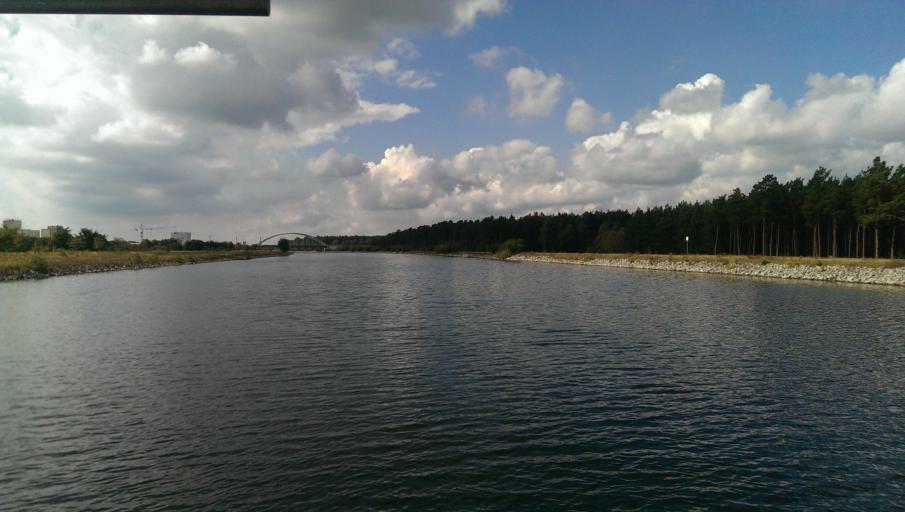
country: DE
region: Brandenburg
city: Eberswalde
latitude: 52.8547
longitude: 13.8091
